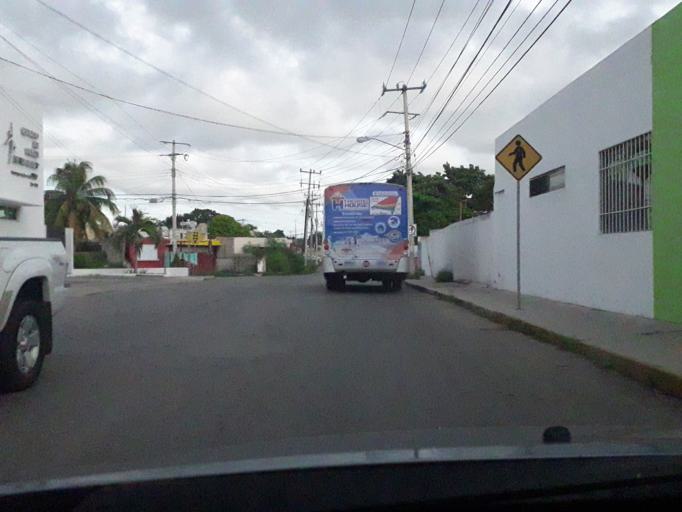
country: MX
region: Yucatan
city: Merida
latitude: 21.0208
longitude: -89.6392
